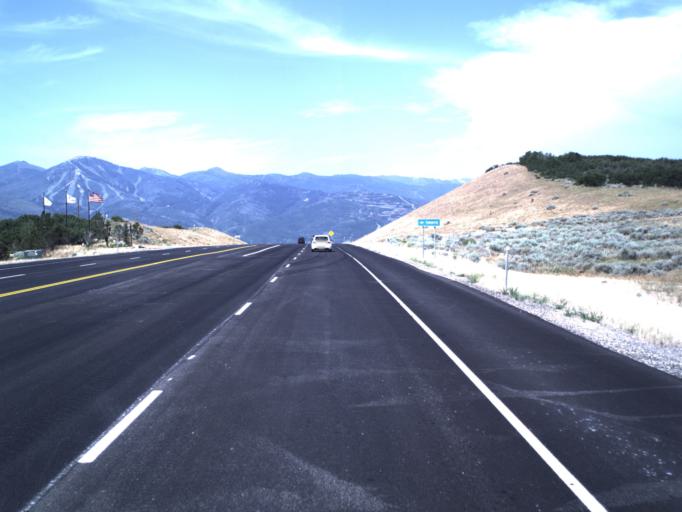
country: US
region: Utah
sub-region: Summit County
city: Kamas
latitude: 40.6342
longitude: -111.3761
